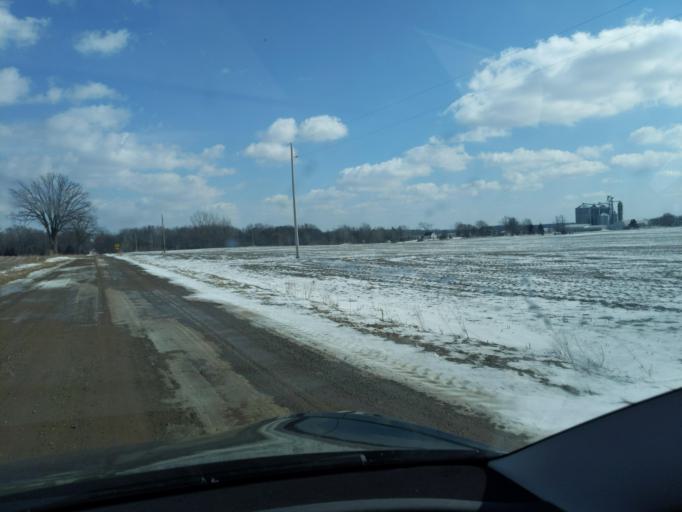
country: US
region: Michigan
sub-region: Ingham County
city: Webberville
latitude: 42.6153
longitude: -84.2286
